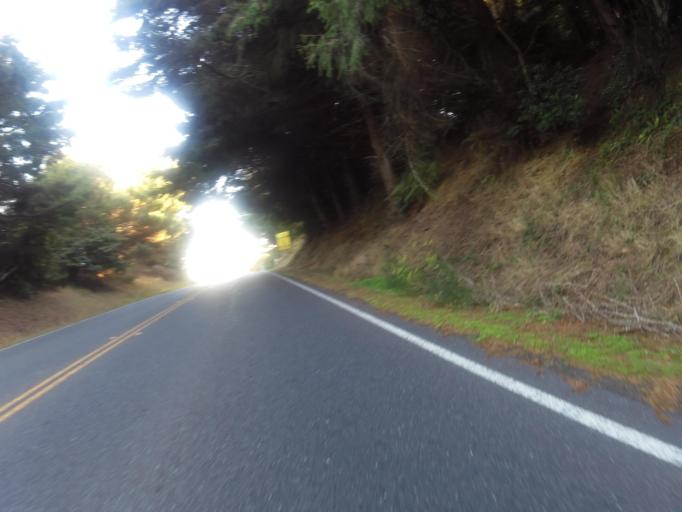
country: US
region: California
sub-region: Sonoma County
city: Sea Ranch
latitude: 38.7567
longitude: -123.5161
